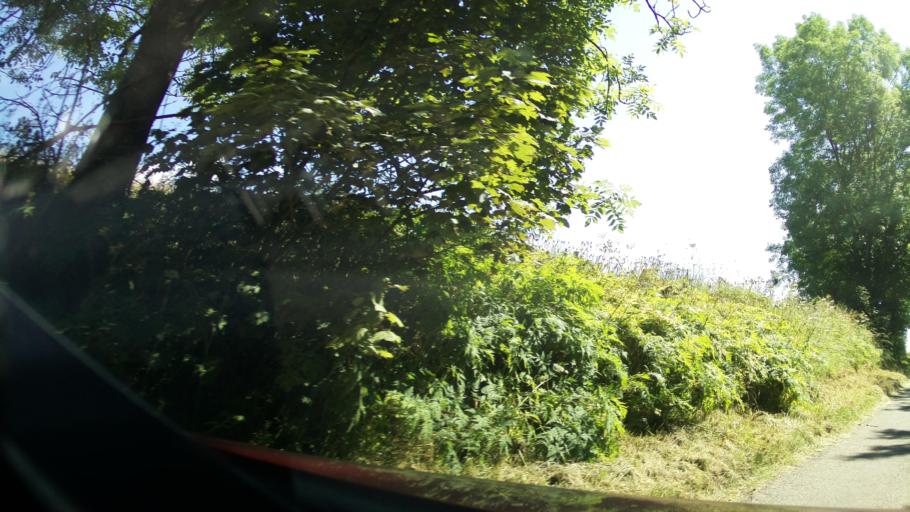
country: GB
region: England
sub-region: Derbyshire
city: Buxton
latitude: 53.2858
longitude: -1.8593
